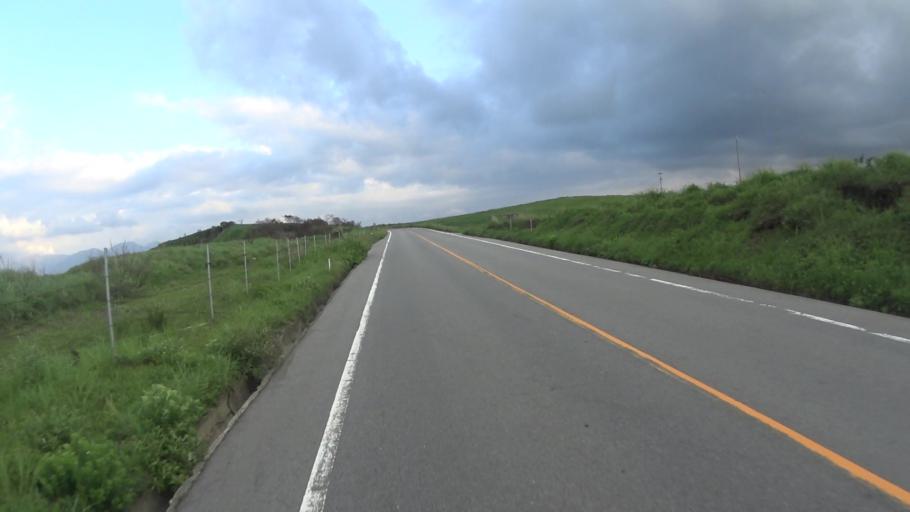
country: JP
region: Kumamoto
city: Aso
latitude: 32.9949
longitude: 131.0118
